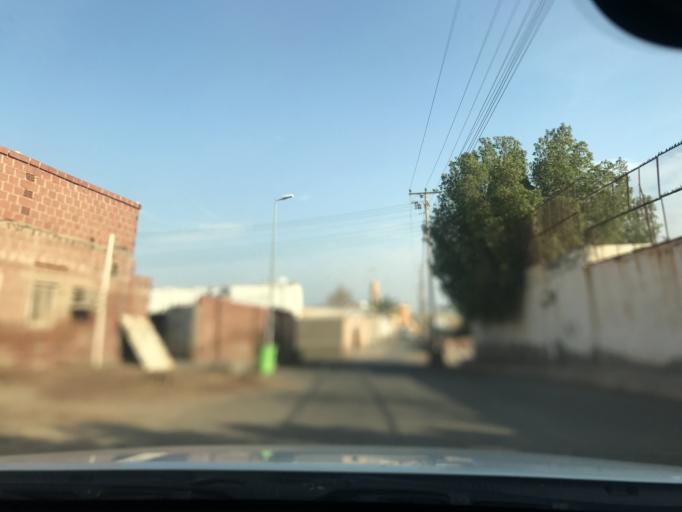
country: SA
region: Makkah
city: Al Jumum
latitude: 21.4463
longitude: 39.5335
